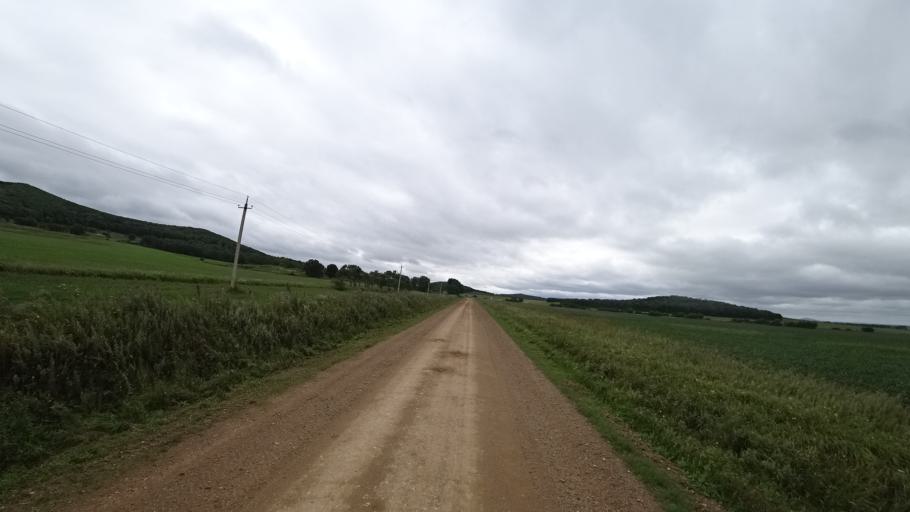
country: RU
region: Primorskiy
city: Chernigovka
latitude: 44.4742
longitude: 132.5803
